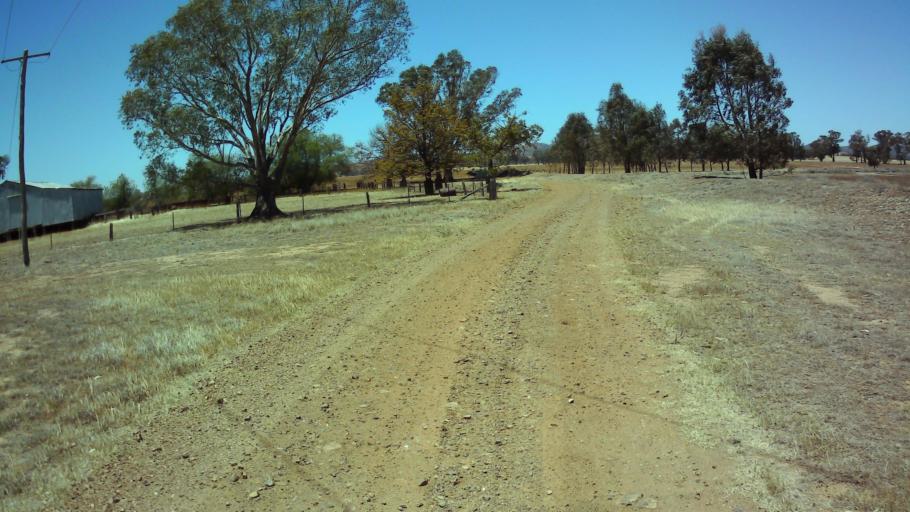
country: AU
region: New South Wales
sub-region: Weddin
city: Grenfell
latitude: -33.7332
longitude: 148.0986
